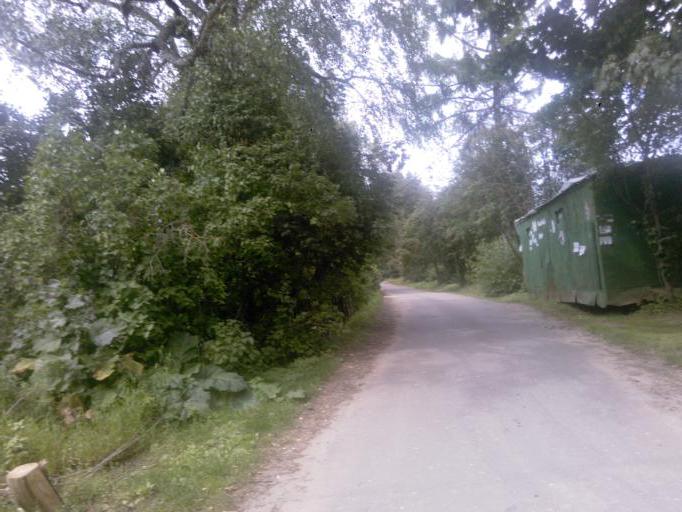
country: RU
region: Moskovskaya
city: Solnechnogorsk
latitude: 56.1478
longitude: 36.9165
